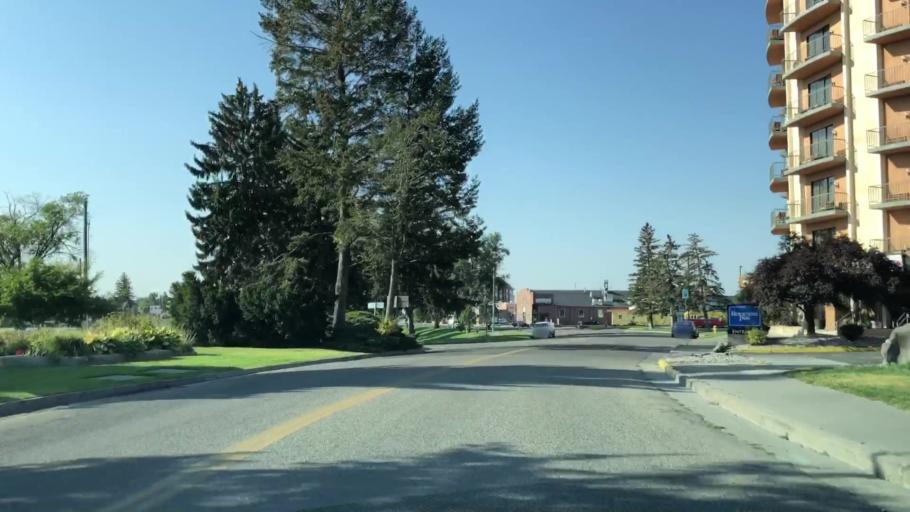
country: US
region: Idaho
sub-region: Bonneville County
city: Idaho Falls
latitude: 43.4968
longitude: -112.0442
